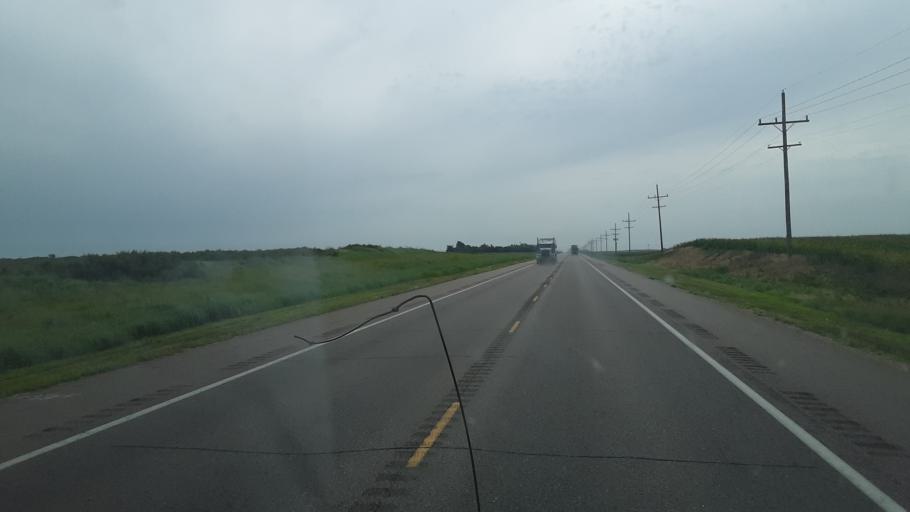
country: US
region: Kansas
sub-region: Edwards County
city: Kinsley
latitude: 37.9275
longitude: -99.3226
